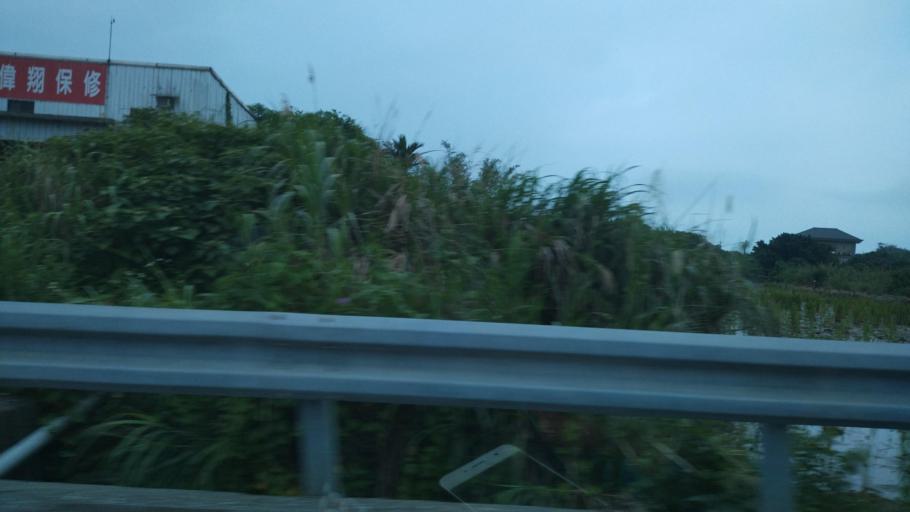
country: TW
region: Taiwan
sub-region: Keelung
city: Keelung
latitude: 25.2101
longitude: 121.6495
